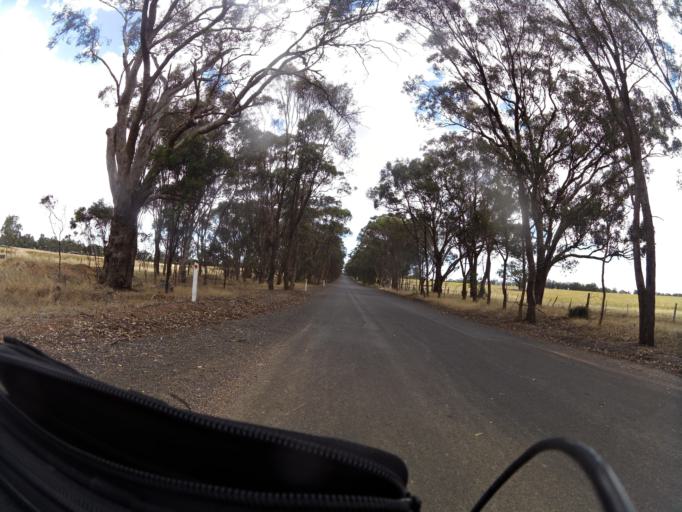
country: AU
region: Victoria
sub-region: Greater Shepparton
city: Shepparton
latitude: -36.7303
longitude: 145.1573
